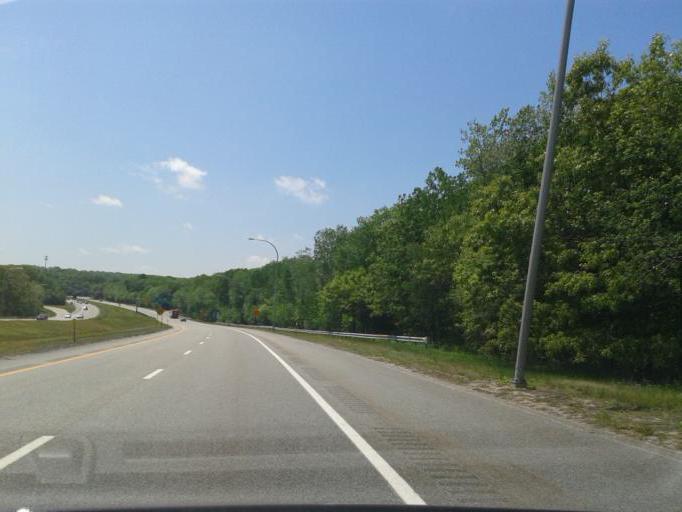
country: US
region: Rhode Island
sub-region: Washington County
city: North Kingstown
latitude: 41.5315
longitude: -71.4575
